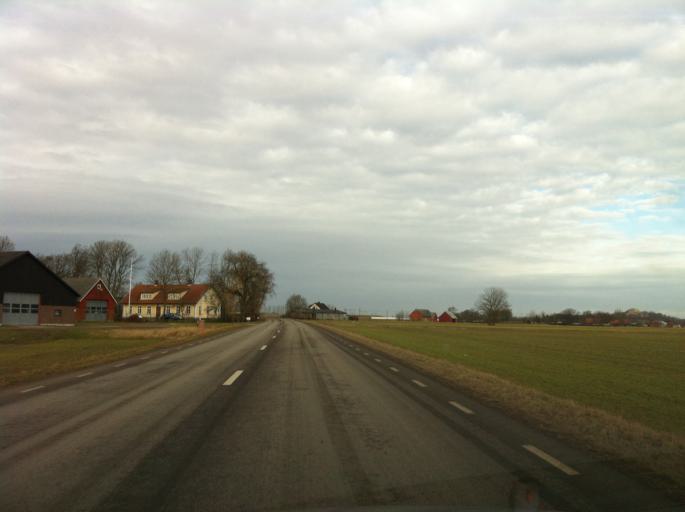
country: SE
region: Skane
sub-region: Bjuvs Kommun
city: Bjuv
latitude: 56.1114
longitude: 12.8935
